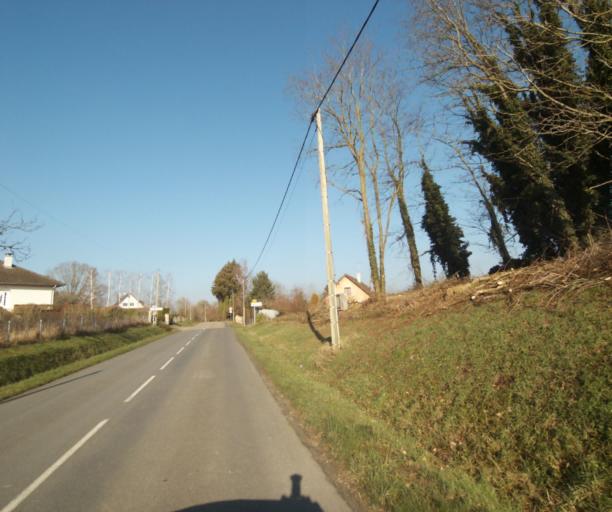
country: FR
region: Champagne-Ardenne
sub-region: Departement de la Haute-Marne
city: Wassy
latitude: 48.4937
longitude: 4.9384
